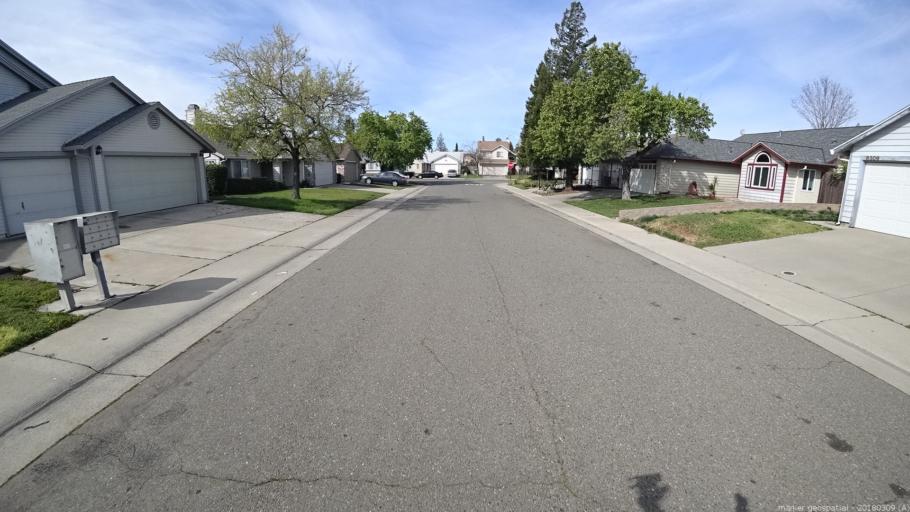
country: US
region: California
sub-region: Sacramento County
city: Florin
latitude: 38.4573
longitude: -121.3984
